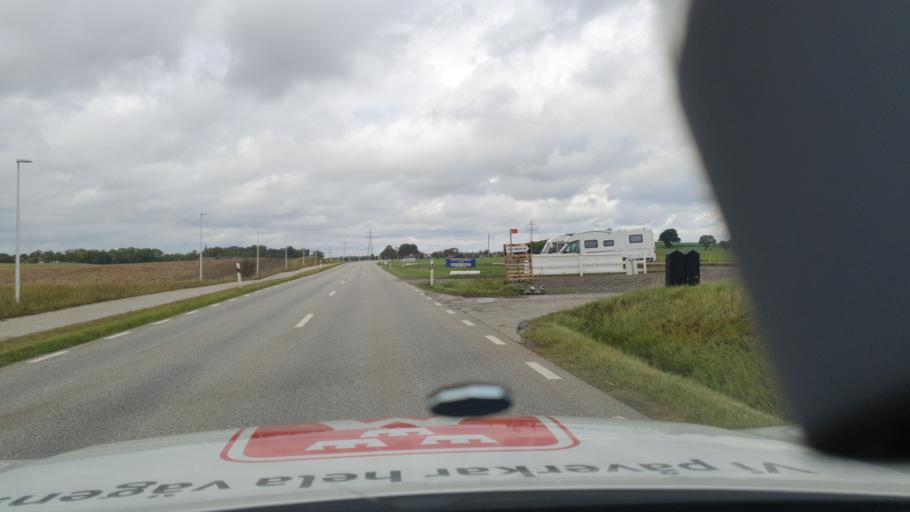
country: SE
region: Skane
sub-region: Malmo
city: Oxie
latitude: 55.5078
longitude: 13.0974
